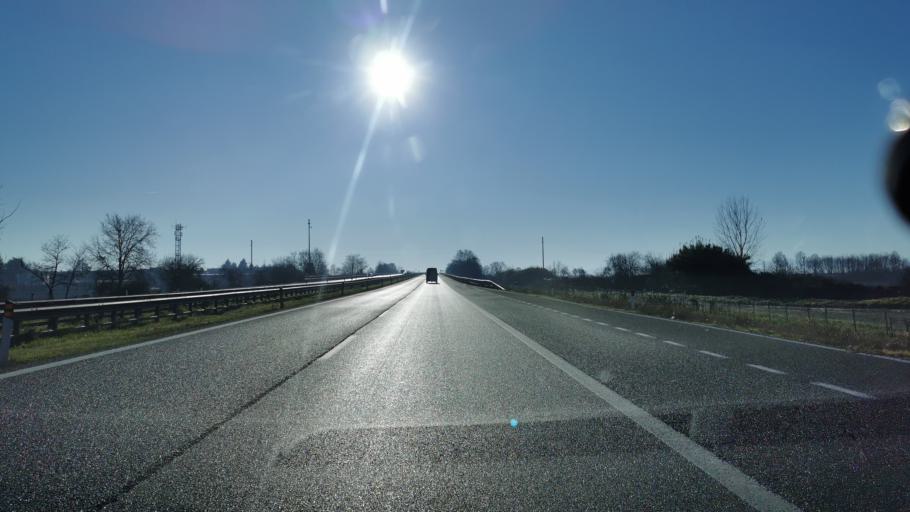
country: IT
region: Piedmont
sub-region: Provincia di Torino
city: Villastellone
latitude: 44.9136
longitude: 7.7377
